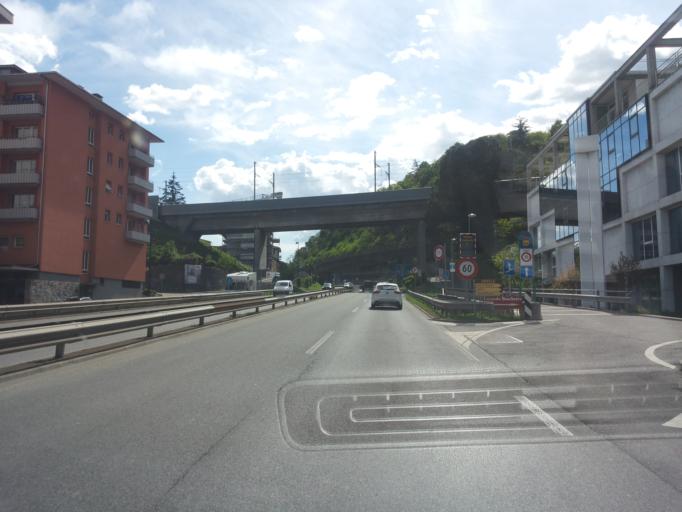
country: CH
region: Ticino
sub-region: Lugano District
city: Sorengo
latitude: 45.9910
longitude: 8.9418
